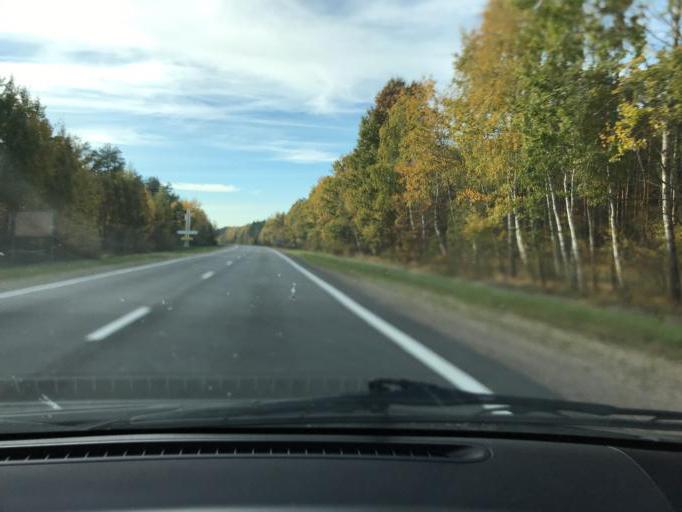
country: BY
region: Brest
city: Ivanava
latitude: 52.1570
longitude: 25.7643
